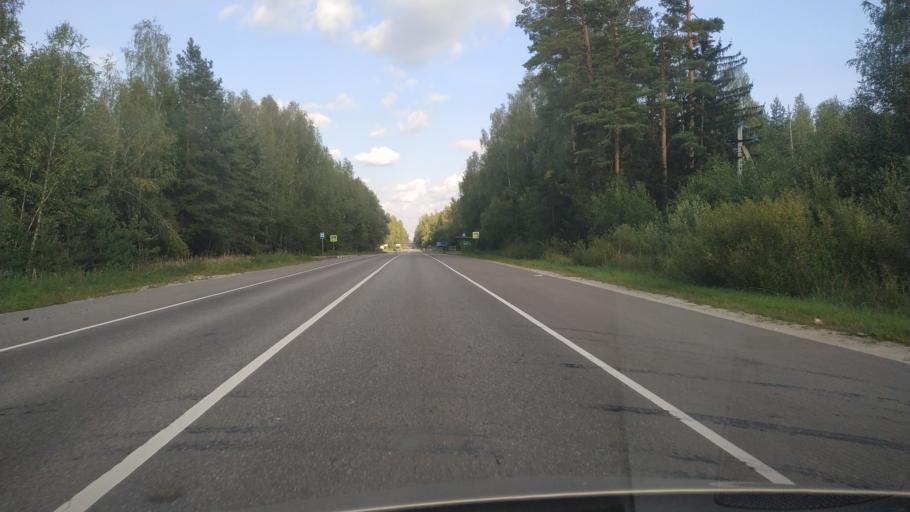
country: RU
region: Moskovskaya
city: Vereya
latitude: 55.7029
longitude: 39.1827
